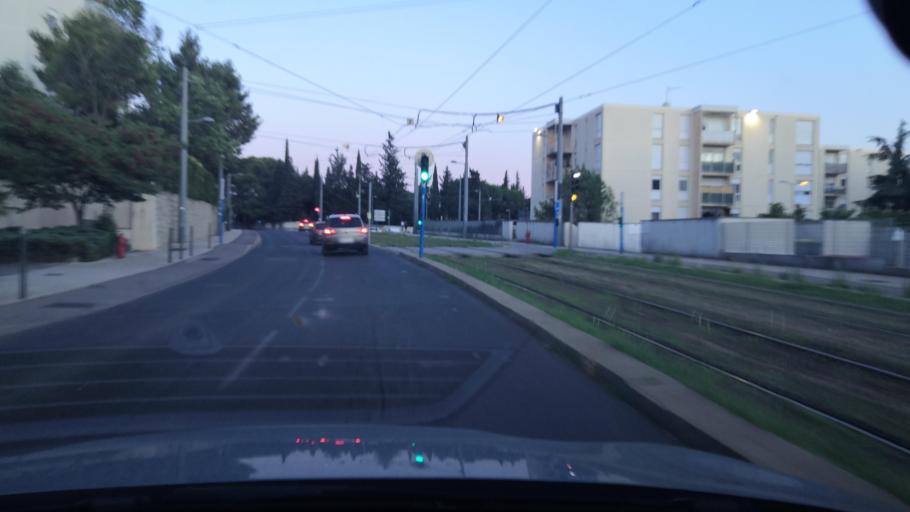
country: FR
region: Languedoc-Roussillon
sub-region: Departement de l'Herault
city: Juvignac
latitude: 43.6171
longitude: 3.8402
